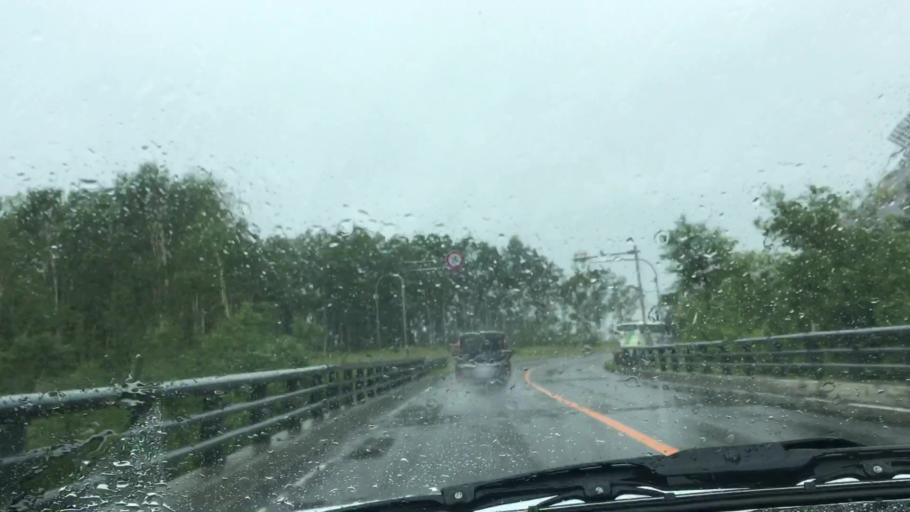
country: JP
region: Hokkaido
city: Sapporo
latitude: 42.8720
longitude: 141.1407
